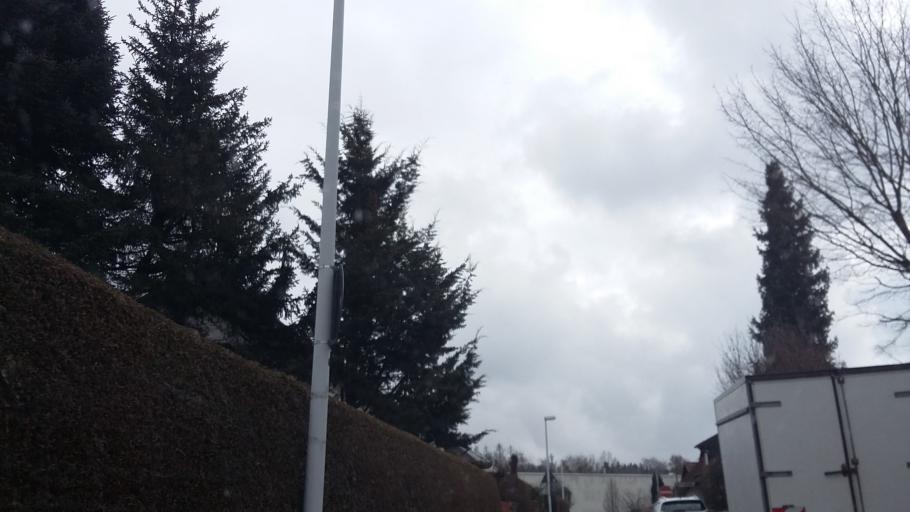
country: DE
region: Bavaria
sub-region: Upper Bavaria
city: Gilching
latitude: 48.1005
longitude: 11.2996
